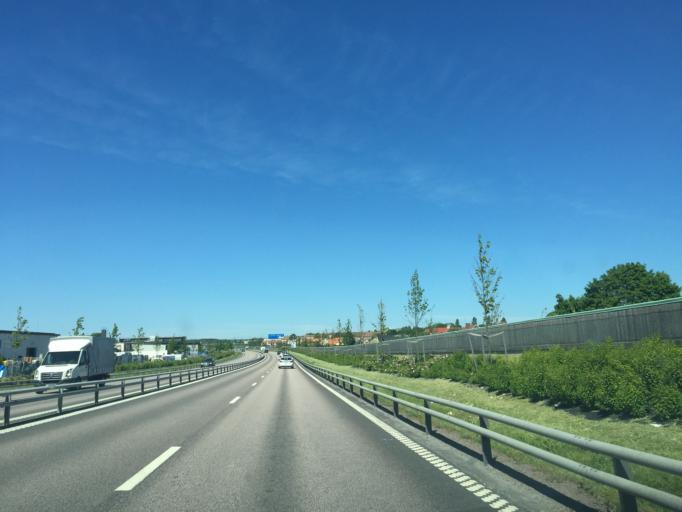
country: SE
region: OEstergoetland
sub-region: Motala Kommun
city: Motala
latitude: 58.5353
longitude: 15.0179
